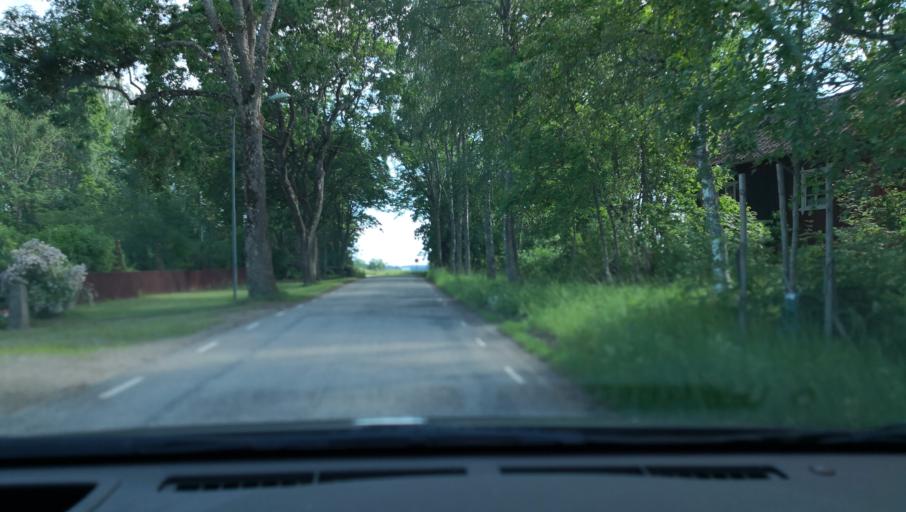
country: SE
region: Uppsala
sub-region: Enkopings Kommun
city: Irsta
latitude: 59.7647
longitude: 16.9874
